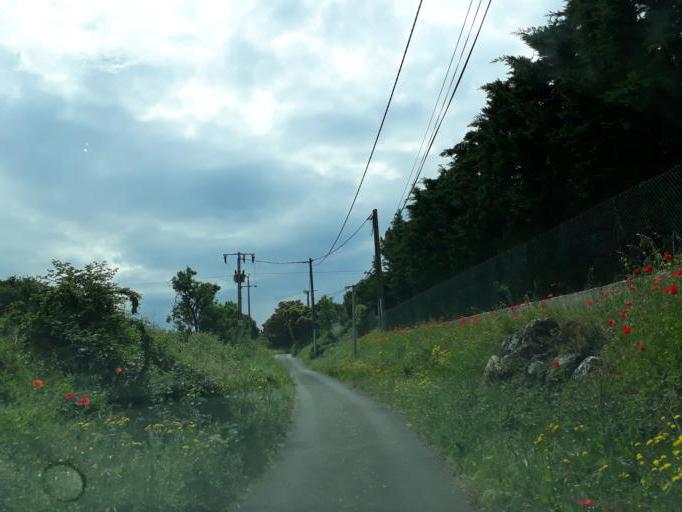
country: FR
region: Languedoc-Roussillon
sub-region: Departement de l'Herault
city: Agde
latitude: 43.2958
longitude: 3.4885
